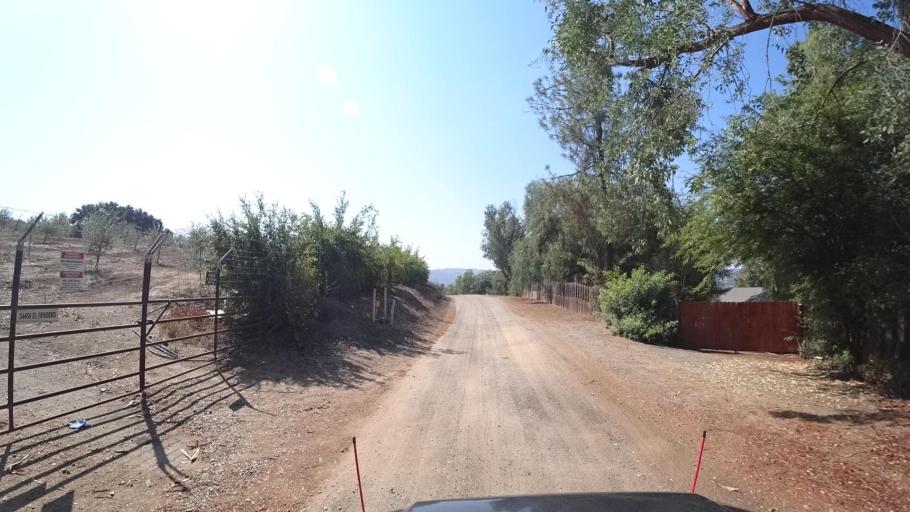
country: US
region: California
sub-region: San Diego County
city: Valley Center
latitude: 33.3386
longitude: -117.0021
